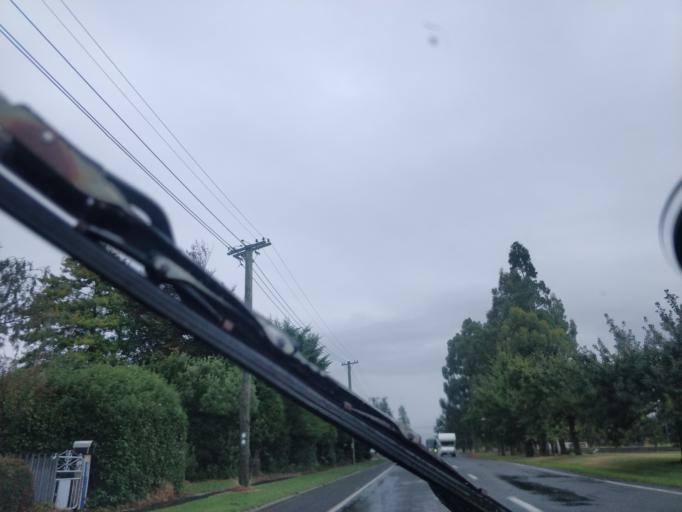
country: NZ
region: Canterbury
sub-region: Selwyn District
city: Darfield
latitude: -43.3879
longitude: 172.0177
